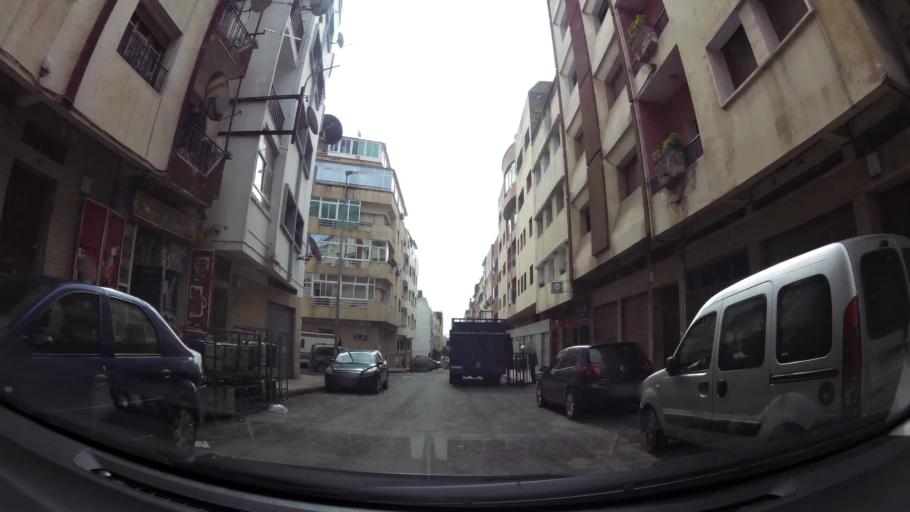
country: MA
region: Grand Casablanca
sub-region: Casablanca
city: Casablanca
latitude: 33.5663
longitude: -7.6704
